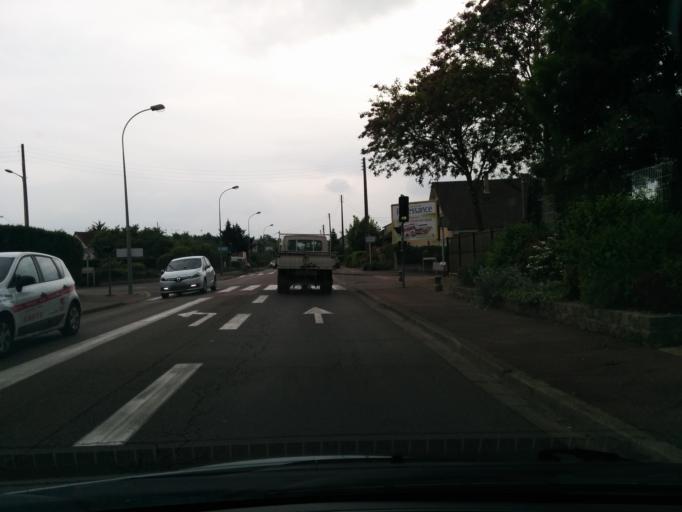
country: FR
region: Ile-de-France
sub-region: Departement des Yvelines
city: Limay
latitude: 48.9946
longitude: 1.7387
